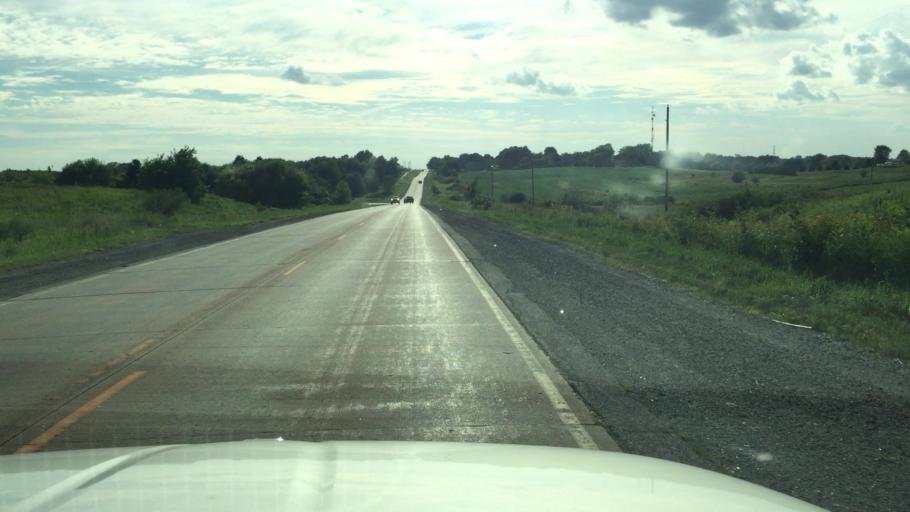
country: US
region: Iowa
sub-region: Johnson County
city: Iowa City
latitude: 41.6710
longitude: -91.4598
